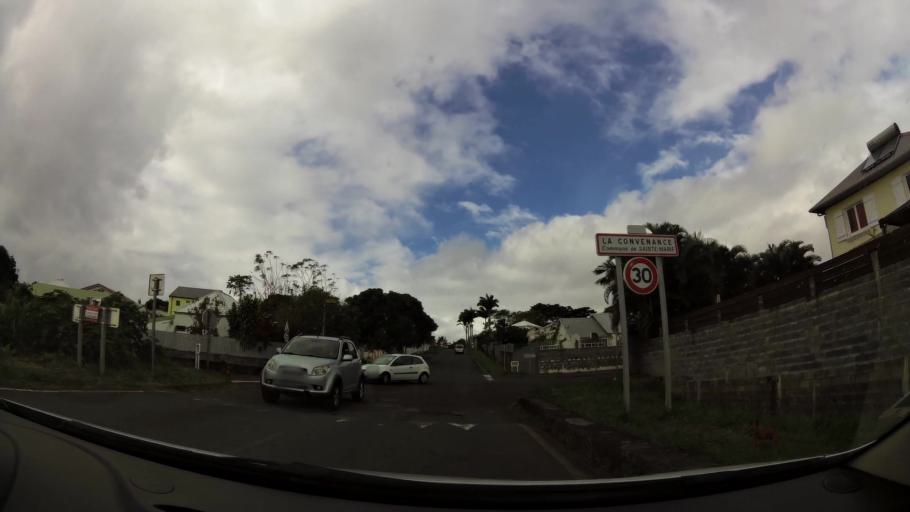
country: RE
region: Reunion
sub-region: Reunion
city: Sainte-Marie
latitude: -20.8956
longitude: 55.5640
